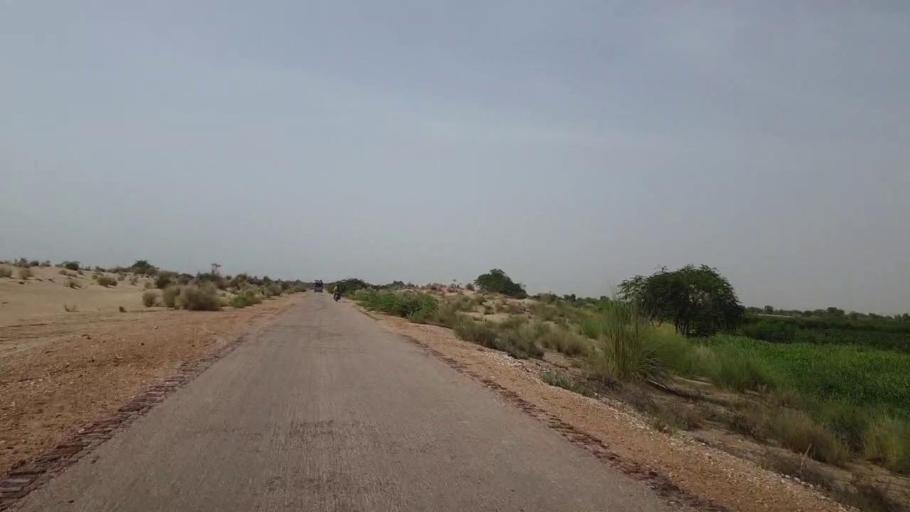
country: PK
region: Sindh
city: Bandhi
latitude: 26.5611
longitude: 68.3818
